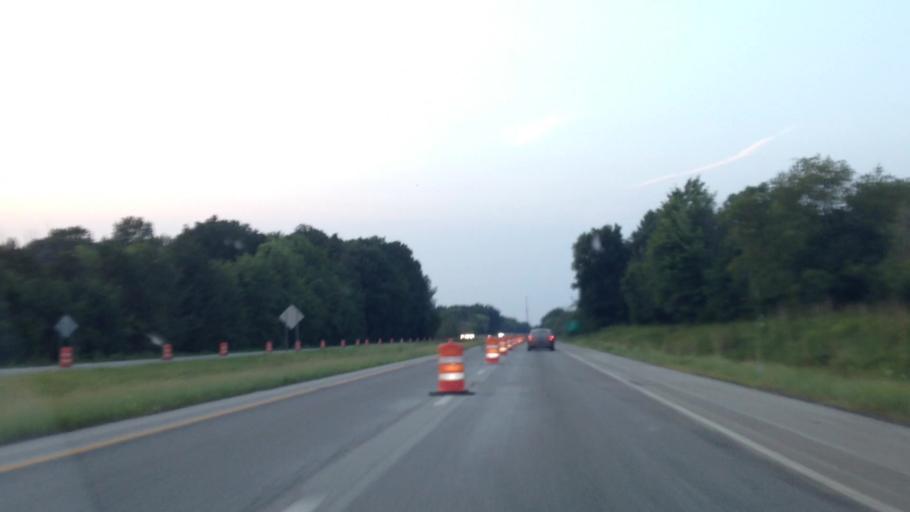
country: US
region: Ohio
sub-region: Wayne County
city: Doylestown
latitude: 40.9730
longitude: -81.6614
